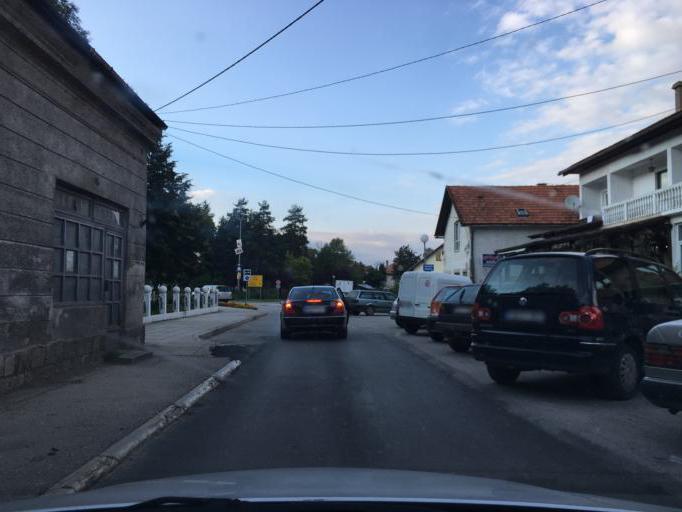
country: BA
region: Federation of Bosnia and Herzegovina
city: Bugojno
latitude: 44.0564
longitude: 17.4494
